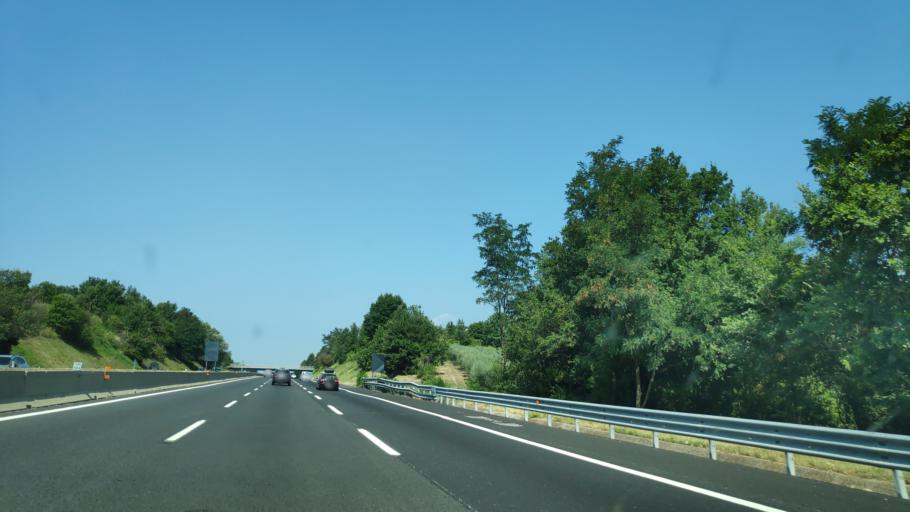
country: IT
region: Campania
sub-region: Provincia di Caserta
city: Mignano Monte Lungo
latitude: 41.4083
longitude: 13.9607
